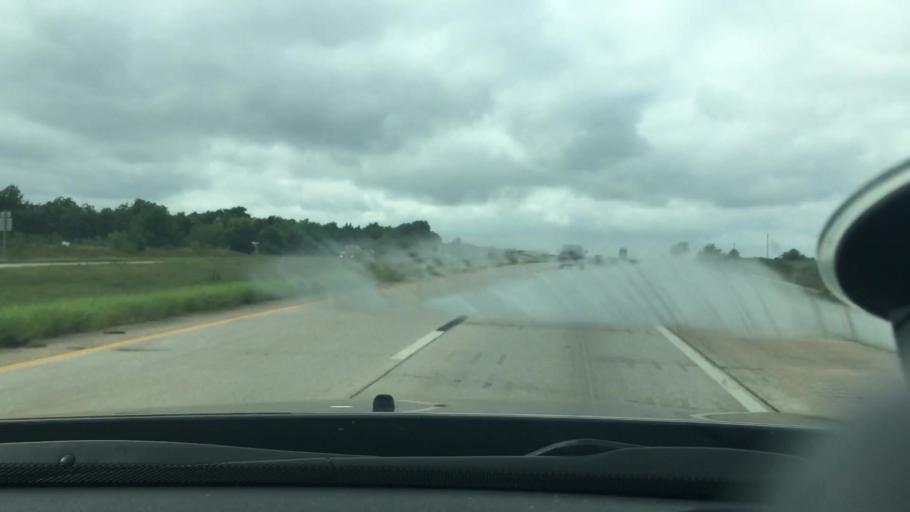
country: US
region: Oklahoma
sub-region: Bryan County
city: Durant
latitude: 34.1402
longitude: -96.2683
